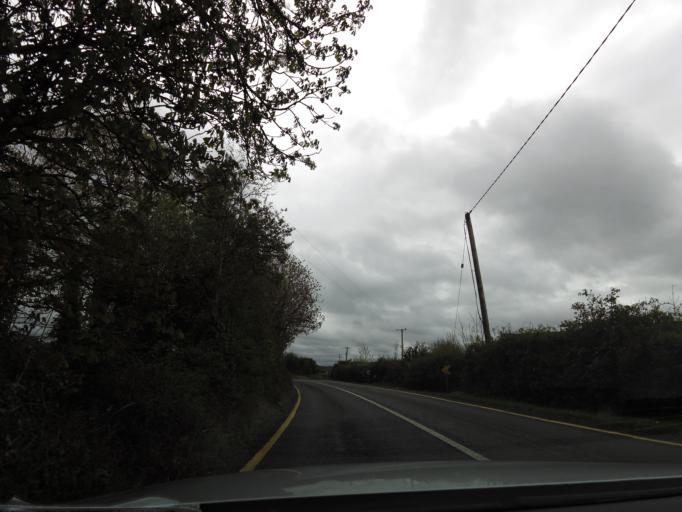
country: IE
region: Leinster
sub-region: Kilkenny
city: Ballyragget
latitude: 52.7207
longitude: -7.3458
